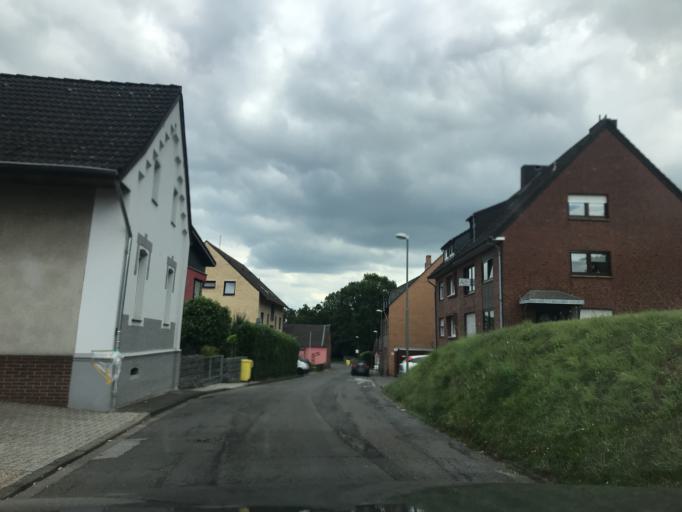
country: DE
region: North Rhine-Westphalia
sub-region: Regierungsbezirk Dusseldorf
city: Neubrueck
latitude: 51.1570
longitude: 6.6706
